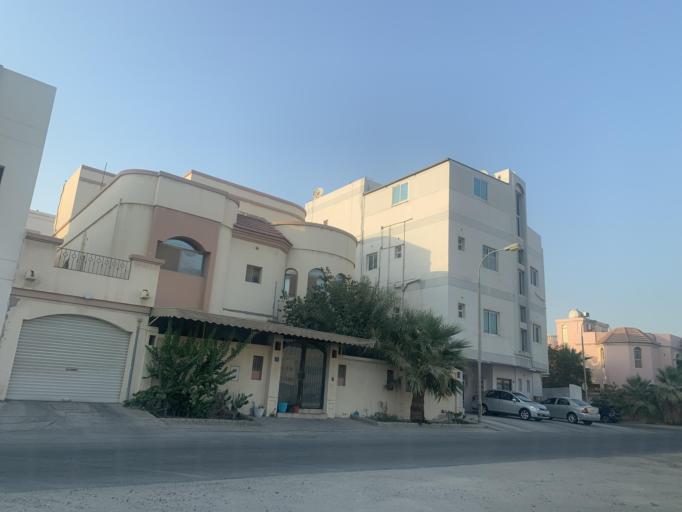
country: BH
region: Manama
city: Jidd Hafs
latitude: 26.2132
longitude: 50.5310
